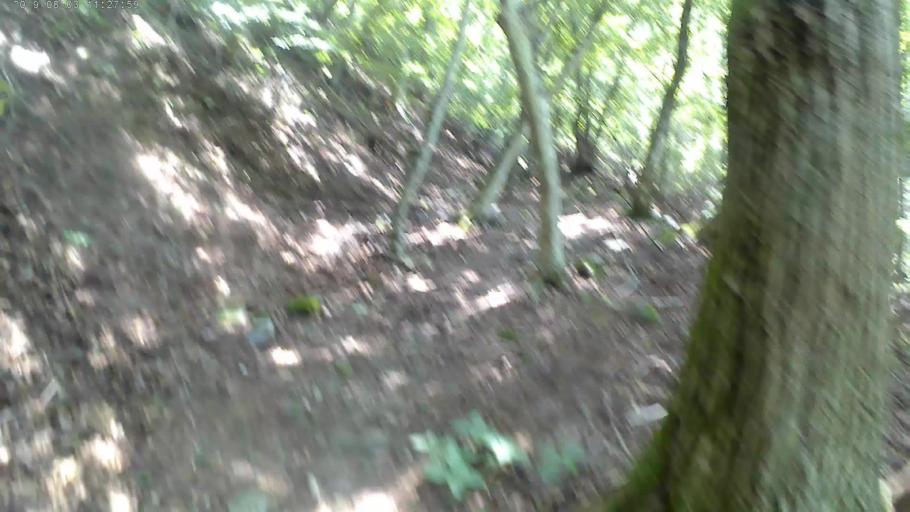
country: JP
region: Yamanashi
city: Enzan
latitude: 35.6137
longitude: 138.7786
